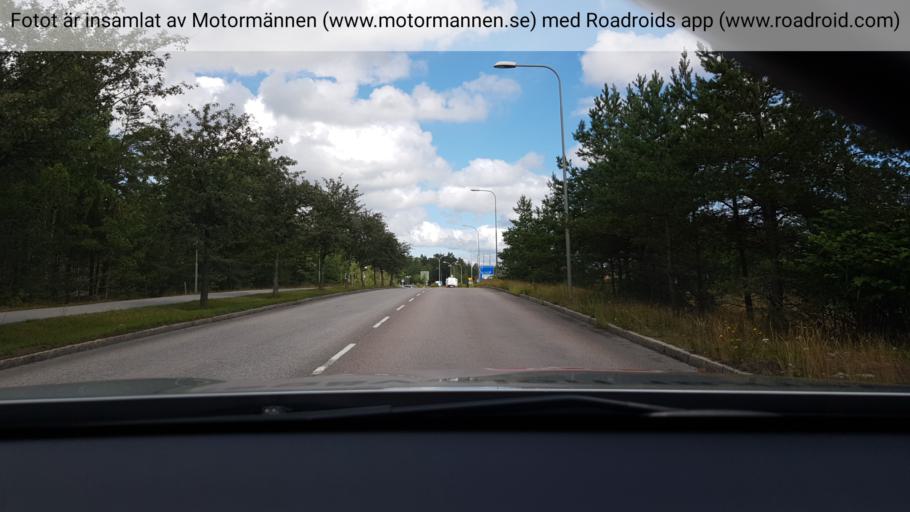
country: SE
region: Stockholm
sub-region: Nacka Kommun
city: Alta
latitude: 59.2409
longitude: 18.1953
